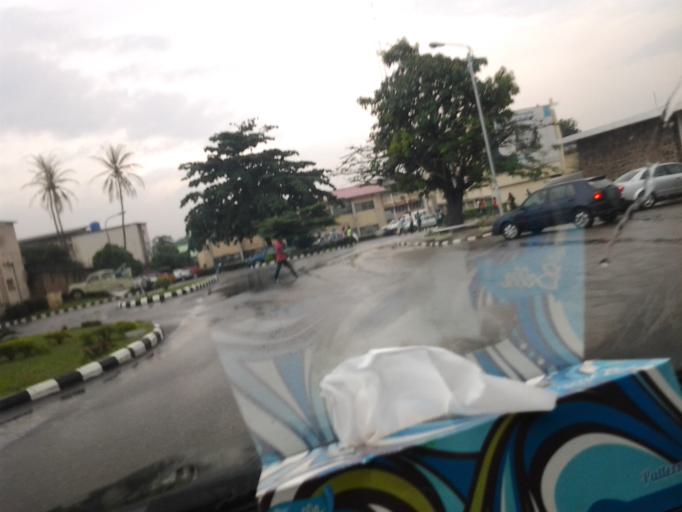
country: NG
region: Oyo
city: Ibadan
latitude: 7.4445
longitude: 3.9007
